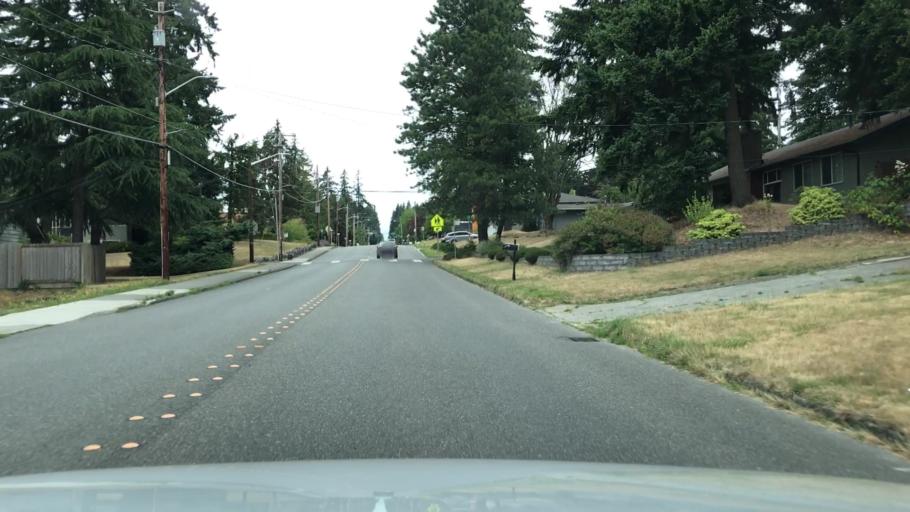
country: US
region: Washington
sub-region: King County
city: Eastgate
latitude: 47.6067
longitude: -122.1322
